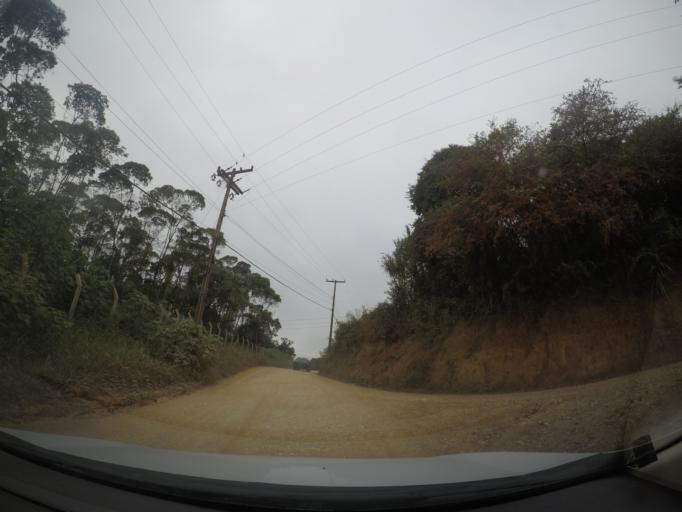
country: BR
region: Parana
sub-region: Colombo
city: Colombo
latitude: -25.3260
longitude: -49.2532
